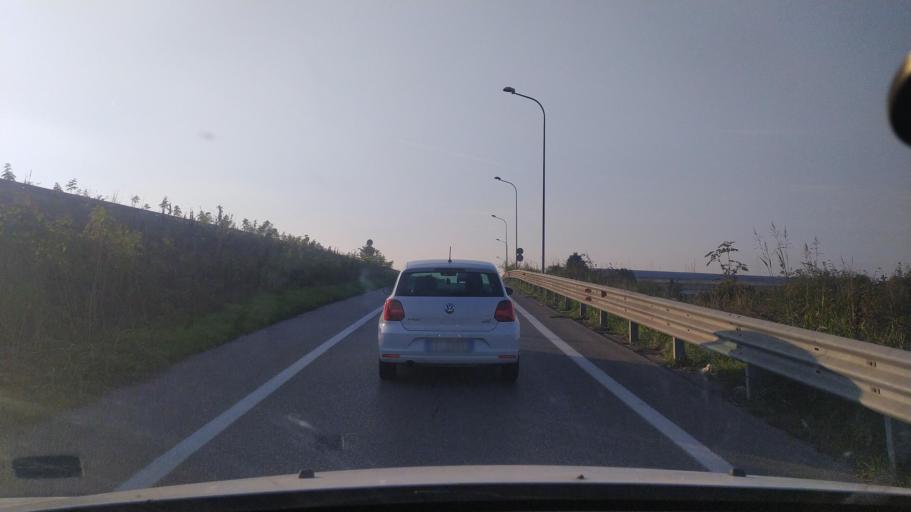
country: IT
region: Lombardy
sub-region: Provincia di Cremona
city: Bagnolo Cremasco
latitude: 45.3634
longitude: 9.6346
